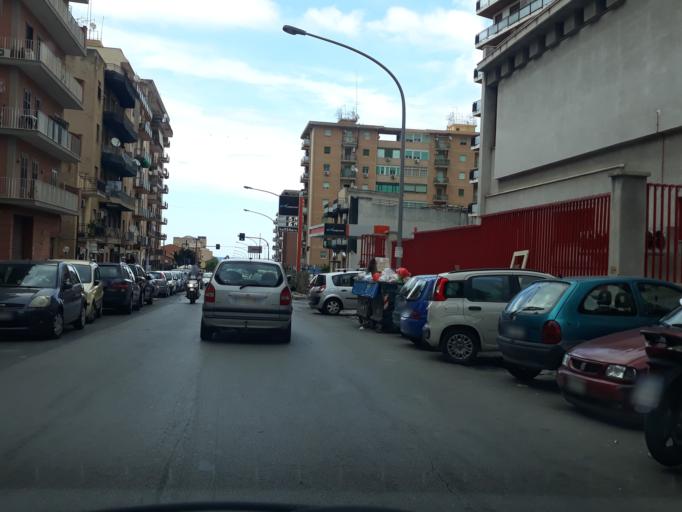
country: IT
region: Sicily
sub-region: Palermo
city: Ciaculli
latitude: 38.0995
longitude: 13.3922
